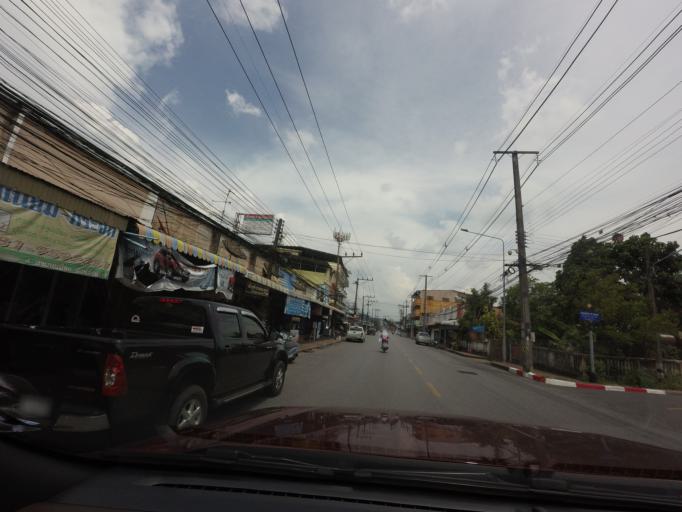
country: TH
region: Yala
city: Yala
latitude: 6.5355
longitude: 101.2865
